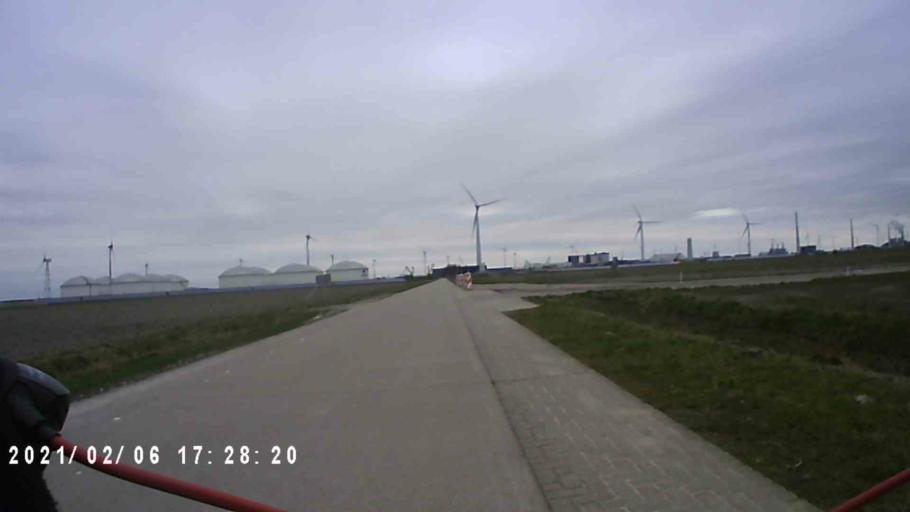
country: NL
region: Groningen
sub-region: Gemeente Appingedam
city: Appingedam
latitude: 53.4412
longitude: 6.8003
